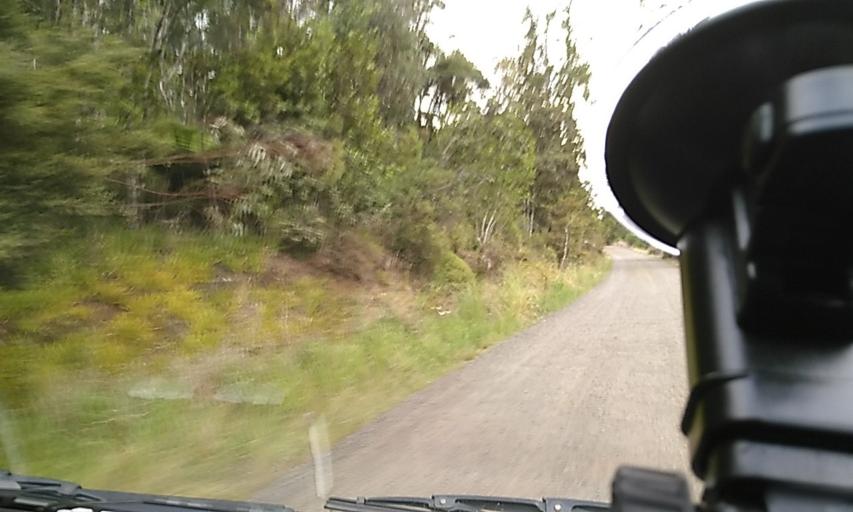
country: NZ
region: Northland
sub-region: Kaipara District
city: Dargaville
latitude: -35.6528
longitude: 173.5553
